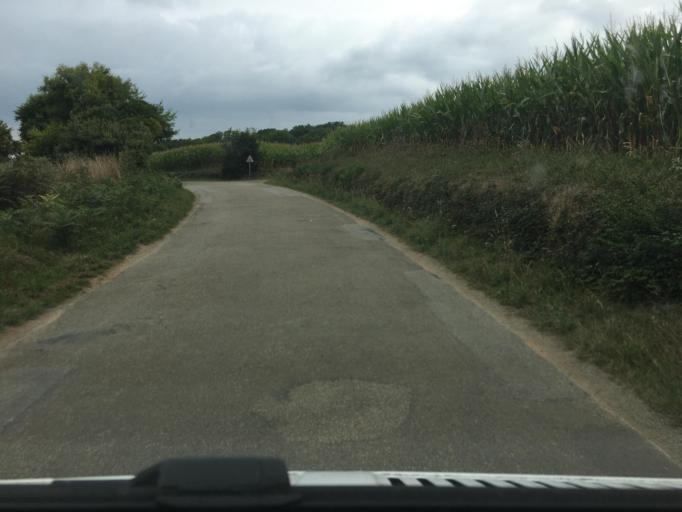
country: FR
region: Brittany
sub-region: Departement du Finistere
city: Beuzec-Cap-Sizun
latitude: 48.0814
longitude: -4.4769
